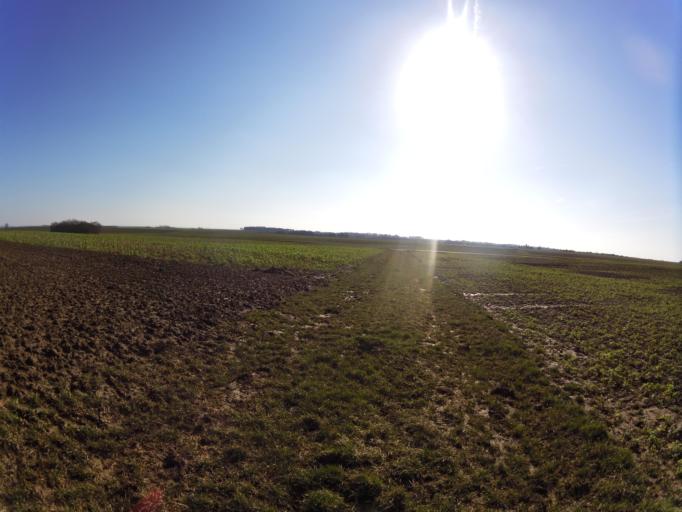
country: DE
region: Bavaria
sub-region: Regierungsbezirk Unterfranken
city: Giebelstadt
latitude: 49.6818
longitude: 9.9696
